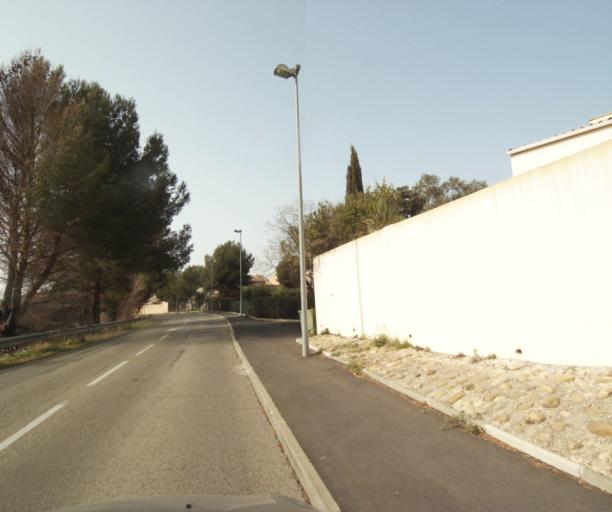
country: FR
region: Provence-Alpes-Cote d'Azur
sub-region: Departement des Bouches-du-Rhone
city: Vitrolles
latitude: 43.4620
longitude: 5.2408
